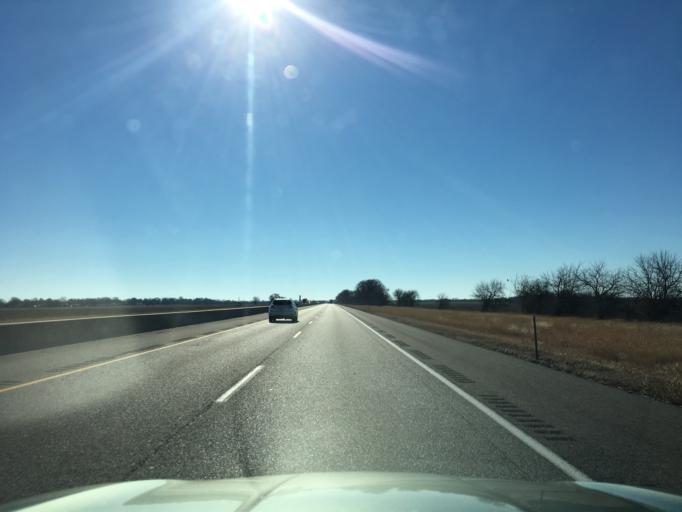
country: US
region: Kansas
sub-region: Sumner County
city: Belle Plaine
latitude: 37.4501
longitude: -97.3223
